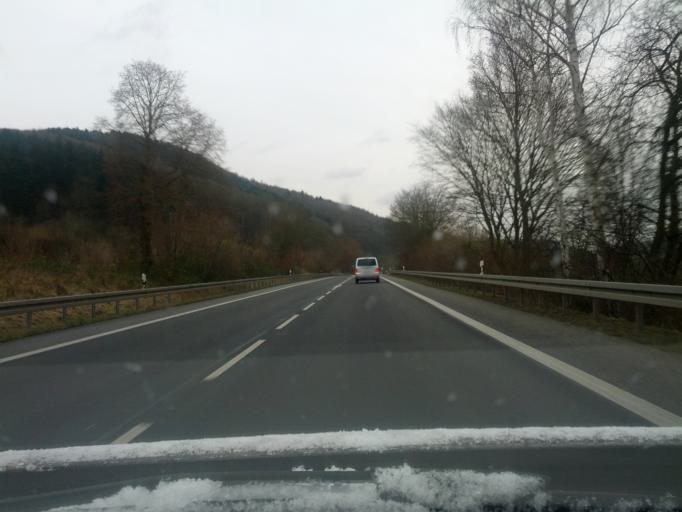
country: DE
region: Thuringia
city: Lindewerra
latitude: 51.3003
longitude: 9.9541
